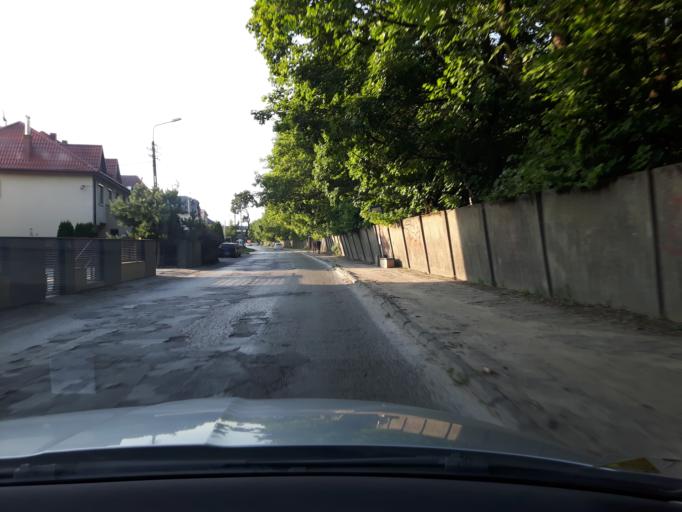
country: PL
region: Masovian Voivodeship
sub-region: Powiat wolominski
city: Zabki
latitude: 52.3044
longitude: 21.1061
